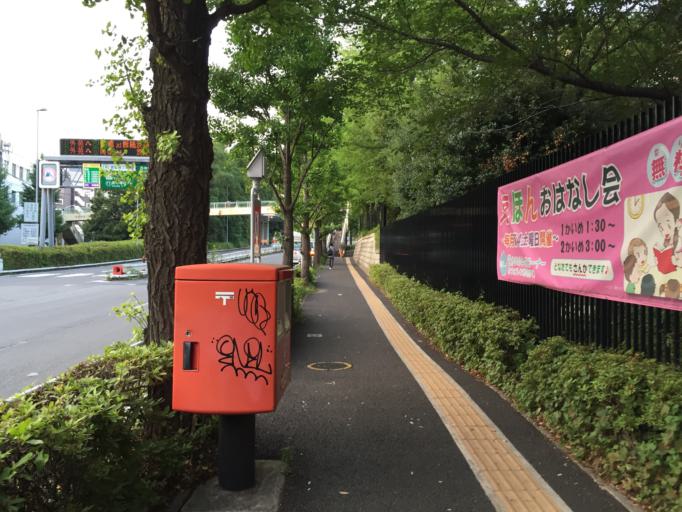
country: JP
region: Tokyo
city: Tokyo
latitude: 35.6759
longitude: 139.6927
